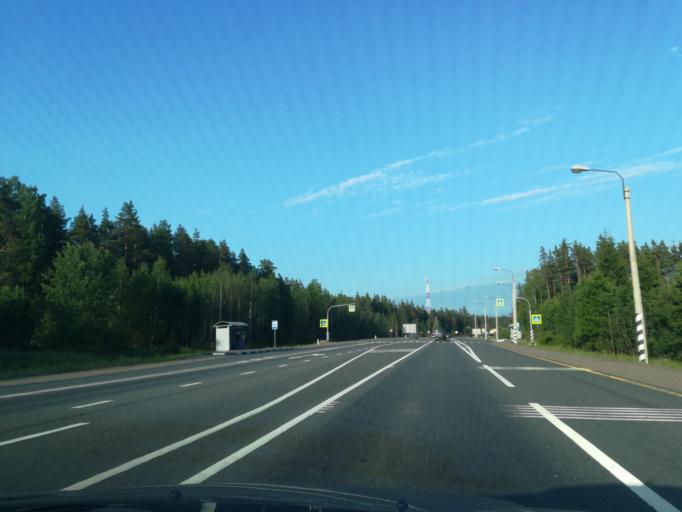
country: RU
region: Leningrad
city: Vyborg
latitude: 60.6684
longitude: 28.9051
